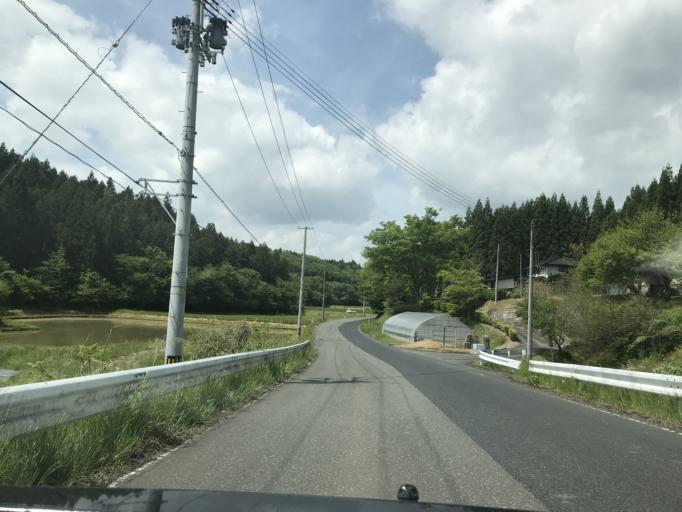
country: JP
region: Miyagi
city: Furukawa
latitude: 38.7730
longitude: 140.9613
